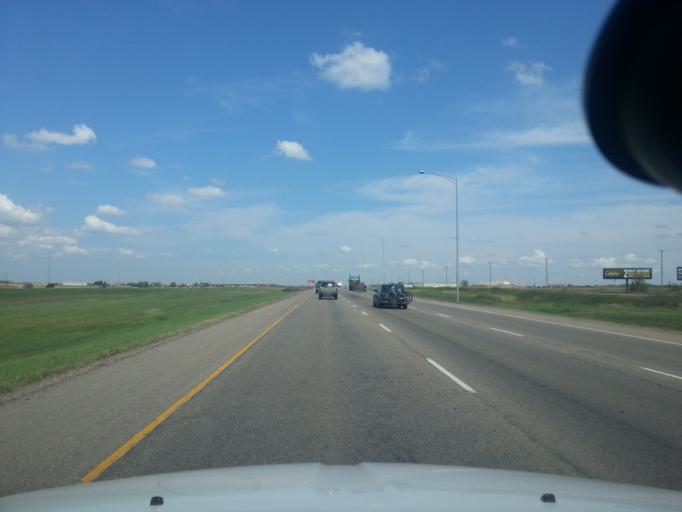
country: CA
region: Alberta
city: Beaumont
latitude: 53.3809
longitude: -113.5189
